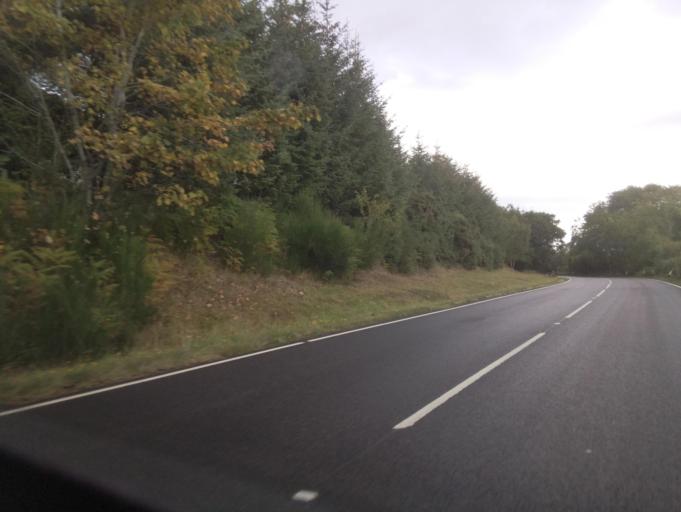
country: GB
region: Scotland
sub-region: Highland
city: Beauly
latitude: 57.4038
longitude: -4.3451
